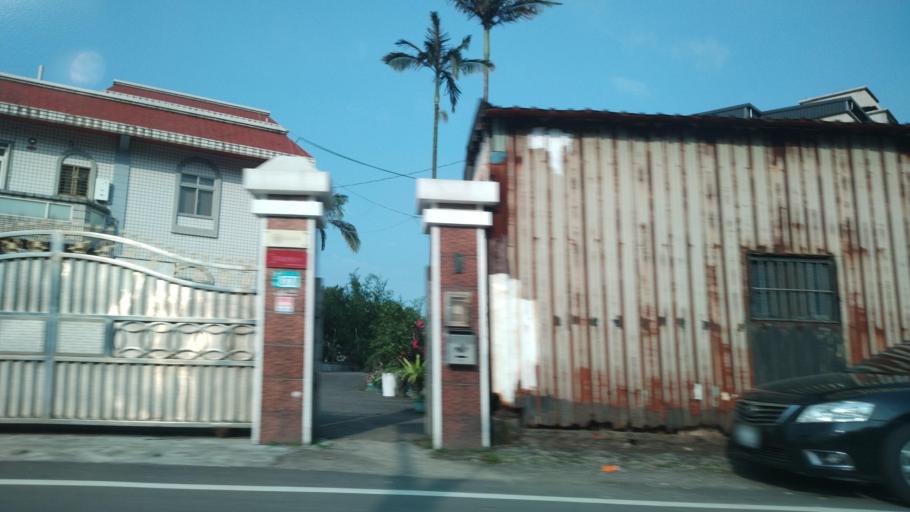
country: TW
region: Taiwan
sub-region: Keelung
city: Keelung
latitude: 25.2225
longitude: 121.6316
